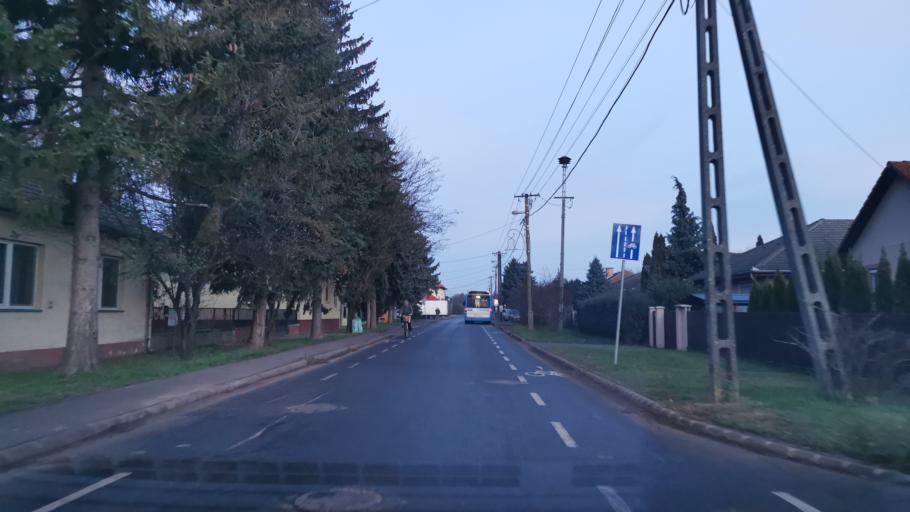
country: HU
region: Hajdu-Bihar
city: Hajduboszormeny
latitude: 47.5928
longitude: 21.5635
